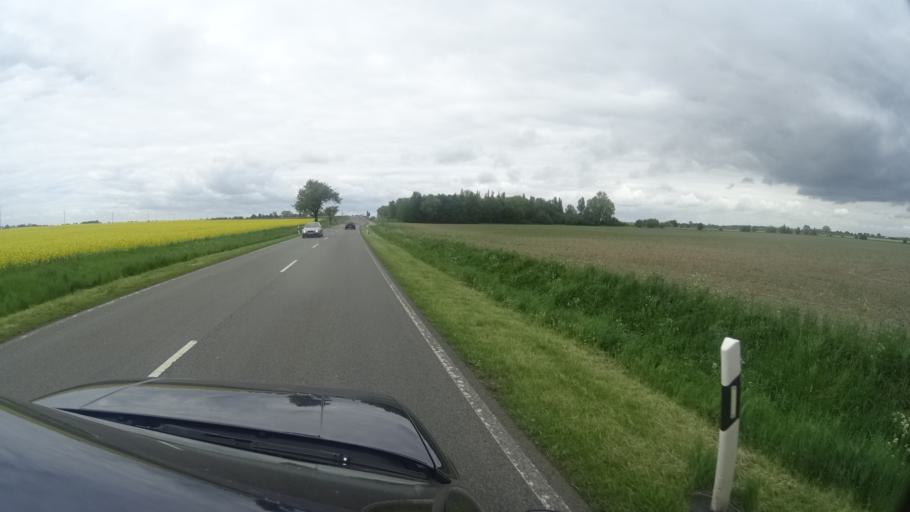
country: DE
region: Brandenburg
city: Fehrbellin
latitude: 52.8431
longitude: 12.7772
